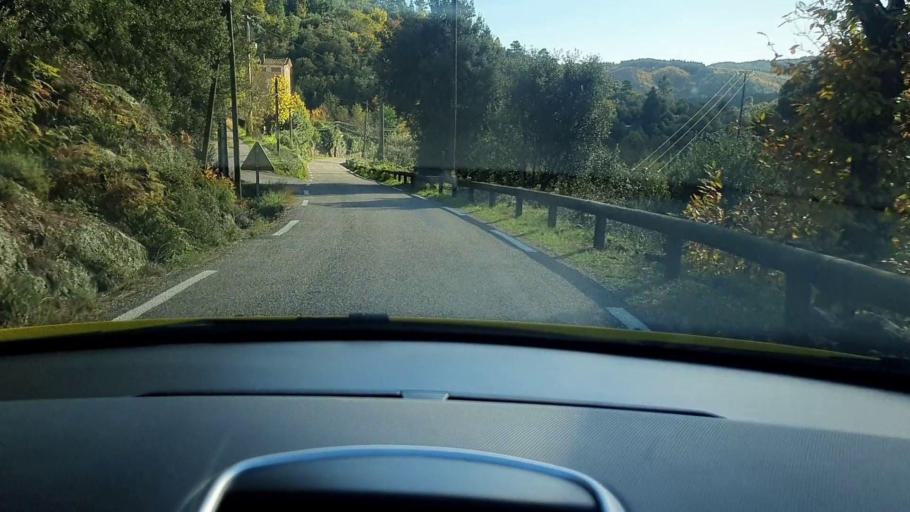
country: FR
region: Languedoc-Roussillon
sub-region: Departement du Gard
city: Lasalle
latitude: 44.0609
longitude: 3.8369
